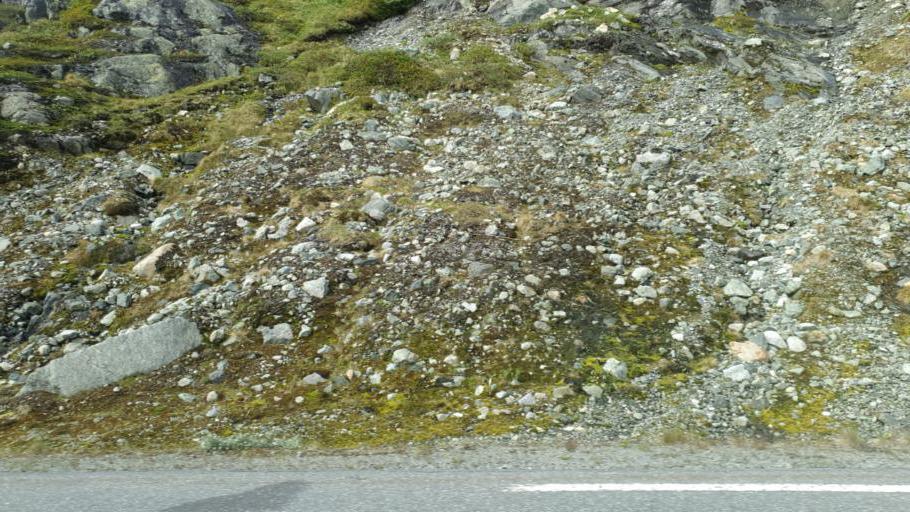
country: NO
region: Oppland
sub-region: Vestre Slidre
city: Slidre
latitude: 61.3404
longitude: 8.8139
